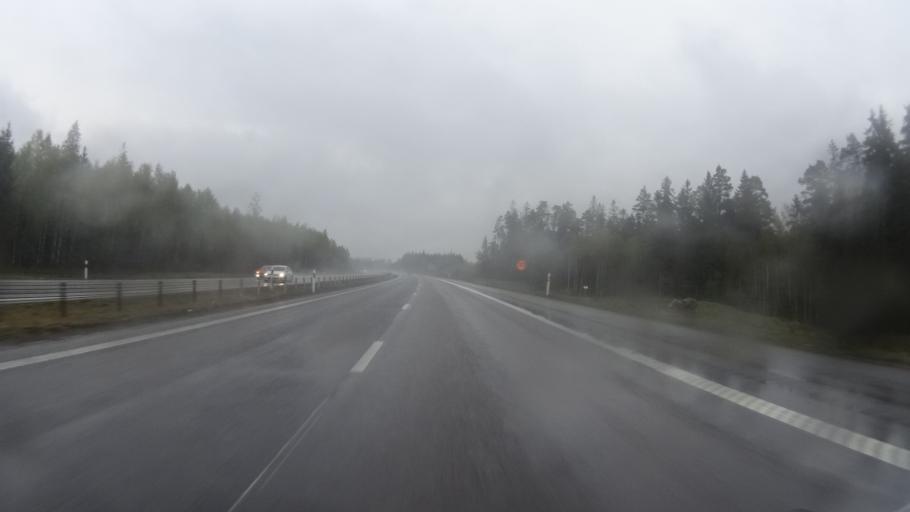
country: SE
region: Kronoberg
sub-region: Markaryds Kommun
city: Stromsnasbruk
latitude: 56.5669
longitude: 13.7220
